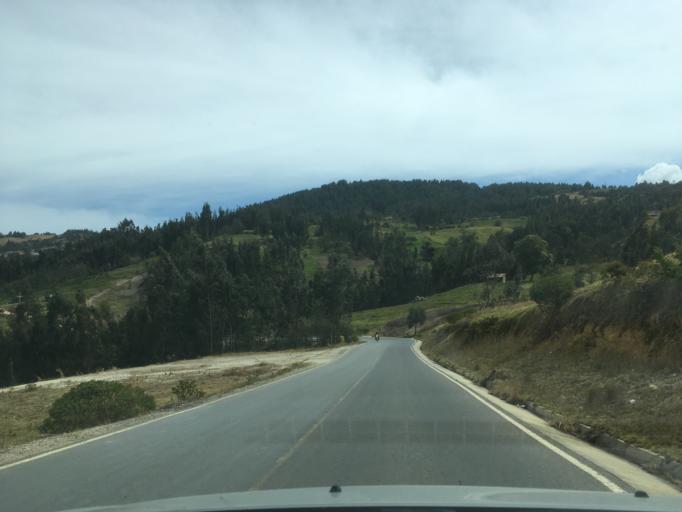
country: CO
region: Boyaca
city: Pesca
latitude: 5.5682
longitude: -72.9737
